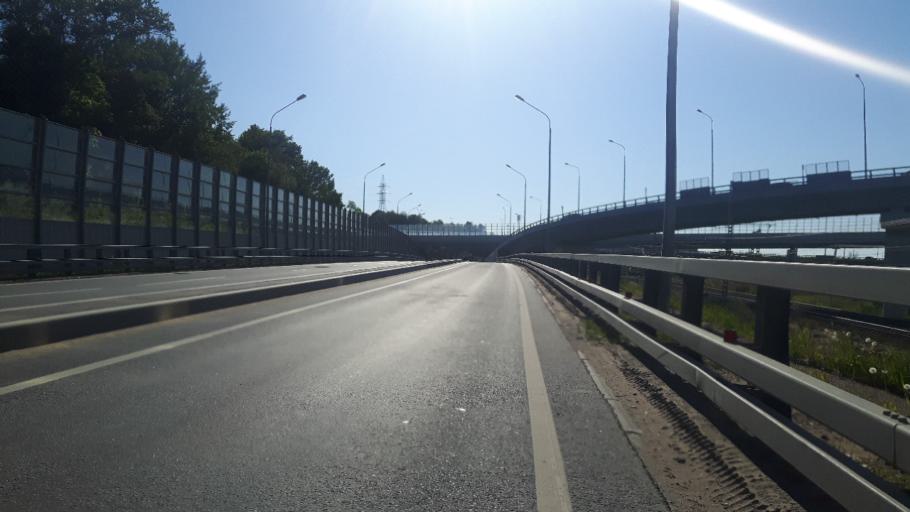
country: RU
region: St.-Petersburg
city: Bol'shaya Izhora
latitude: 59.9266
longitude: 29.6734
